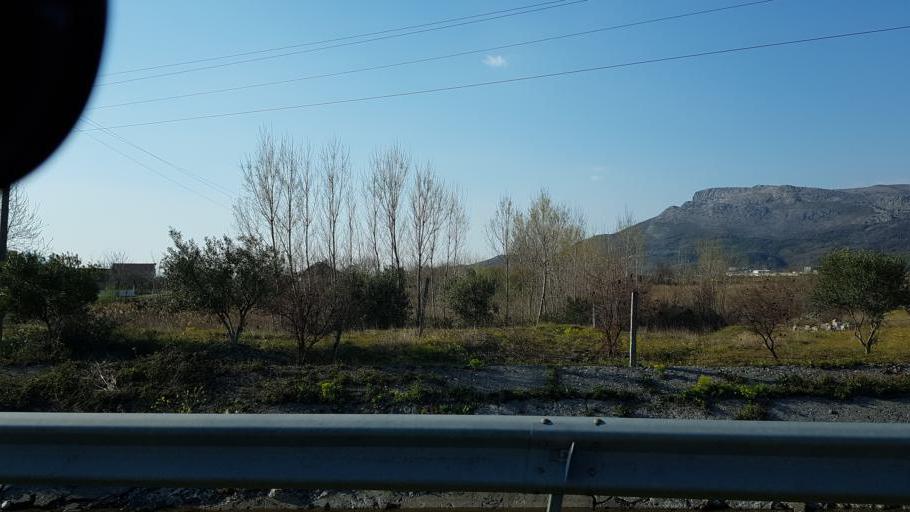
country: AL
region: Shkoder
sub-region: Rrethi i Shkodres
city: Vau i Dejes
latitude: 41.9921
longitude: 19.6032
